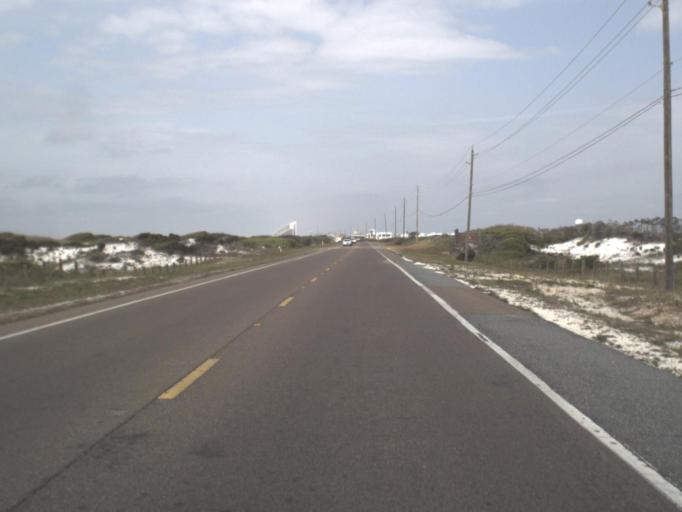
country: US
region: Alabama
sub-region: Baldwin County
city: Orange Beach
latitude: 30.2935
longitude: -87.4561
